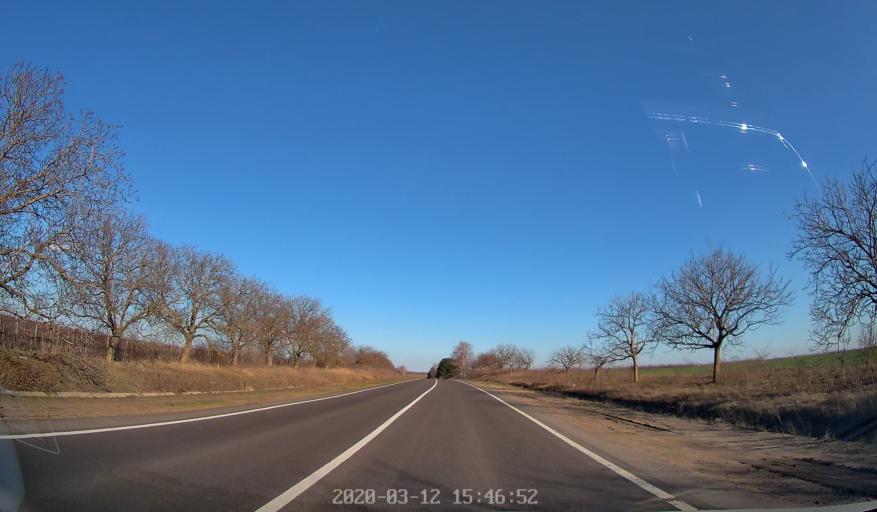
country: MD
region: Chisinau
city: Stauceni
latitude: 47.0976
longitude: 28.9003
